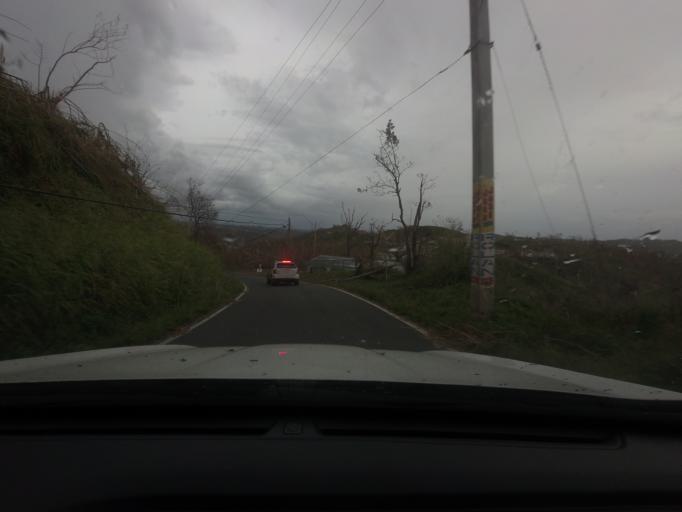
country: PR
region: Ciales
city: Ciales
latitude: 18.2756
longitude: -66.4797
